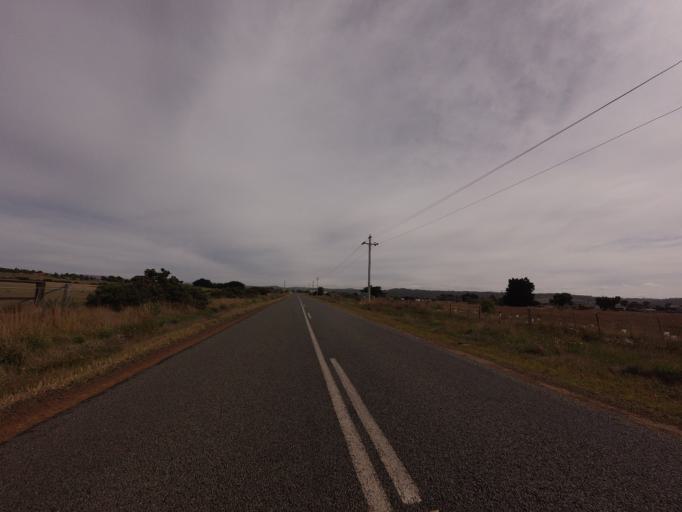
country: AU
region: Tasmania
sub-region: Brighton
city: Bridgewater
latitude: -42.3154
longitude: 147.3738
